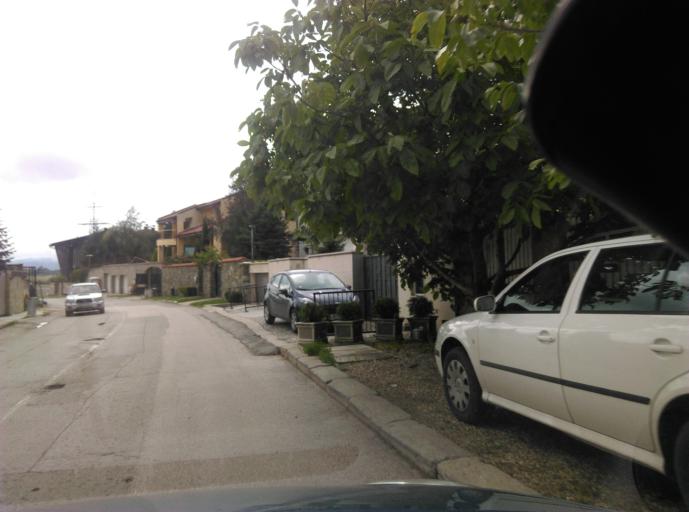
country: BG
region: Sofia-Capital
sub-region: Stolichna Obshtina
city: Sofia
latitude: 42.5901
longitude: 23.3665
